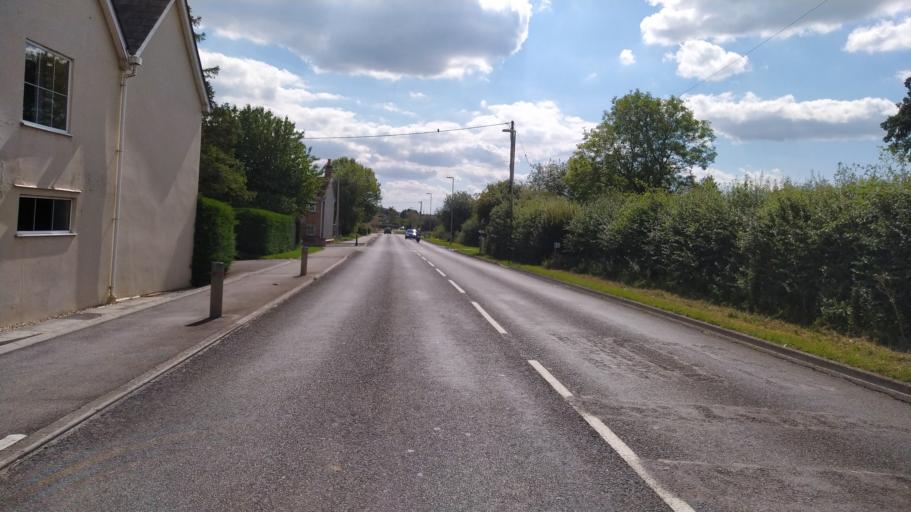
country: GB
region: England
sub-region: Dorset
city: Gillingham
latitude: 51.0508
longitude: -2.2823
